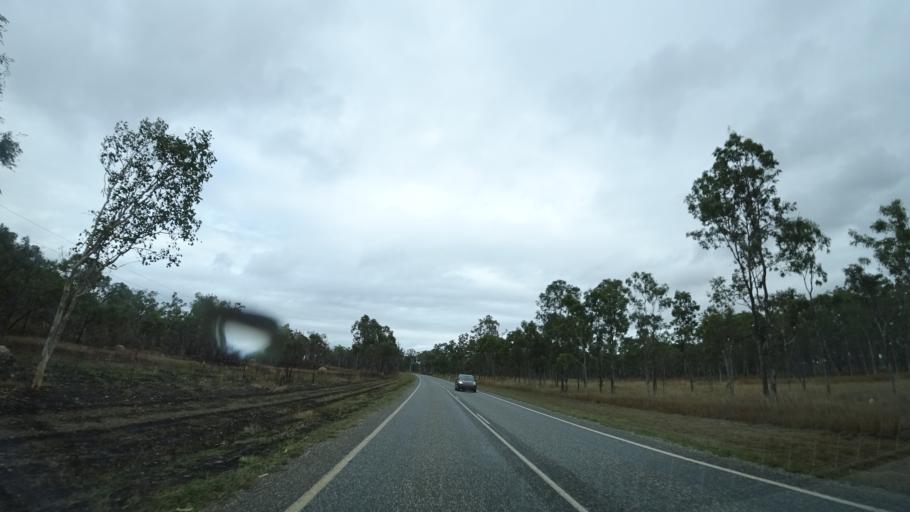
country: AU
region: Queensland
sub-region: Tablelands
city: Mareeba
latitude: -16.7447
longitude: 145.3457
